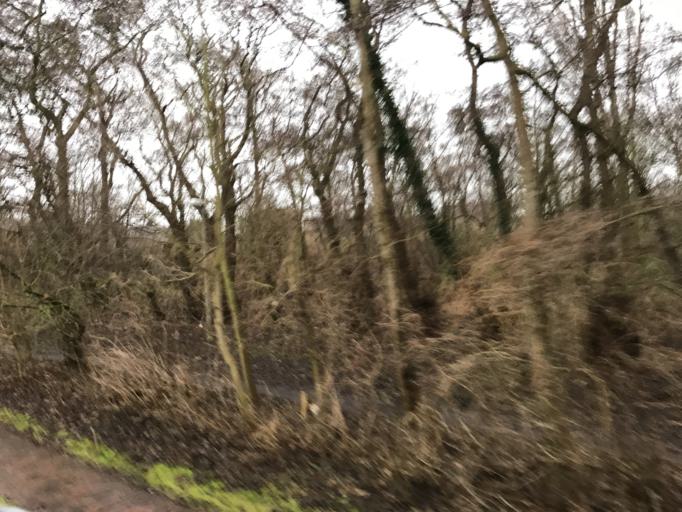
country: DE
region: Lower Saxony
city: Borkum
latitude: 53.5798
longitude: 6.6749
